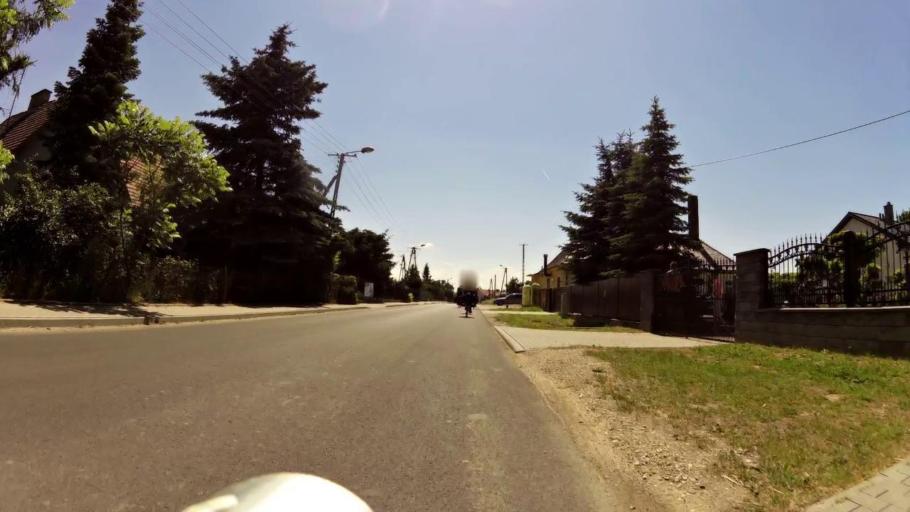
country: PL
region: Kujawsko-Pomorskie
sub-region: Powiat nakielski
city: Slesin
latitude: 53.1673
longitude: 17.7044
